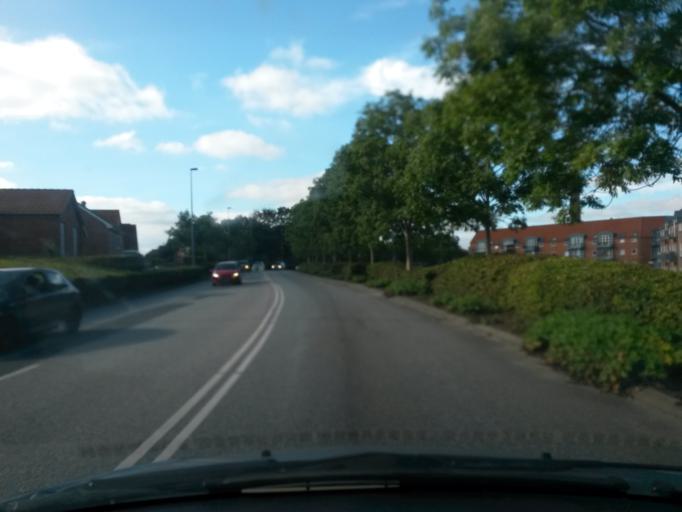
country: DK
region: Central Jutland
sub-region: Holstebro Kommune
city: Holstebro
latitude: 56.3541
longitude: 8.6177
